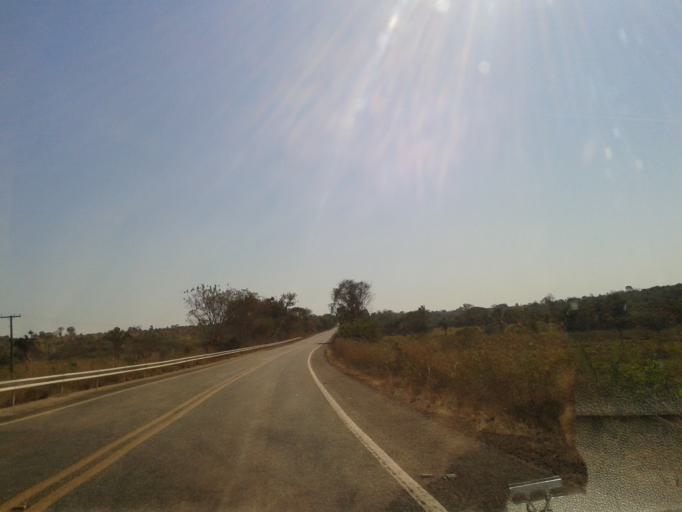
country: BR
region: Goias
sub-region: Mozarlandia
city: Mozarlandia
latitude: -14.4936
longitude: -50.4837
